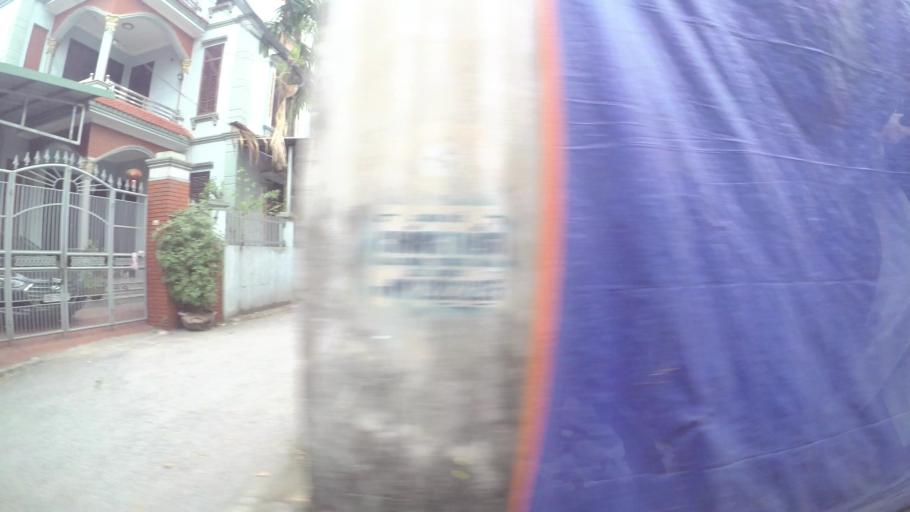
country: VN
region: Ha Noi
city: Trau Quy
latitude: 21.0700
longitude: 105.9197
